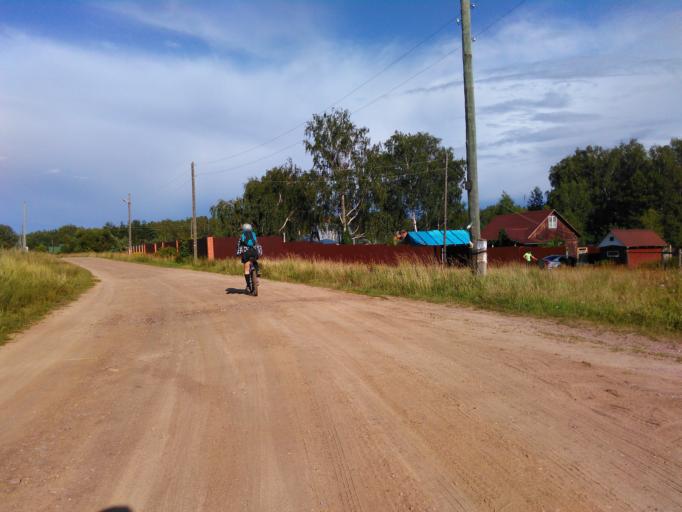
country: RU
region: Vladimir
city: Pokrov
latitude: 55.9690
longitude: 39.1002
